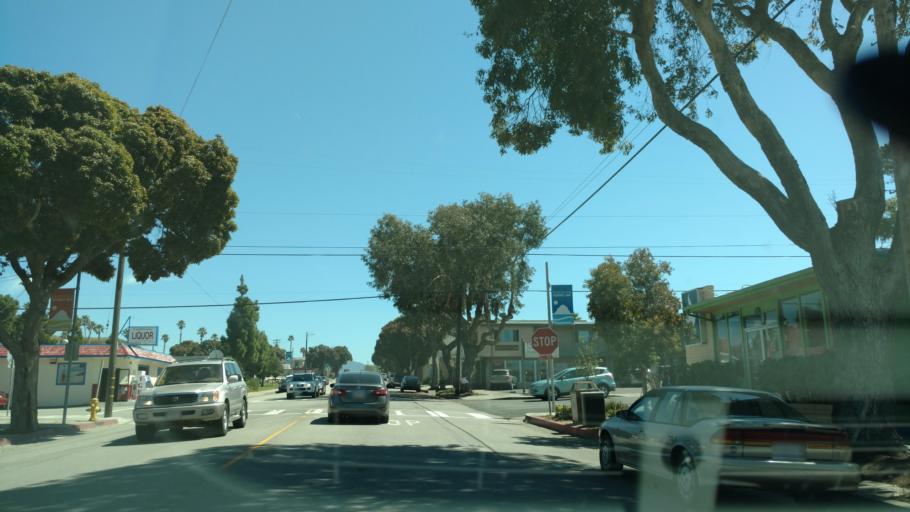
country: US
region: California
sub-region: San Luis Obispo County
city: Morro Bay
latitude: 35.3660
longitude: -120.8459
